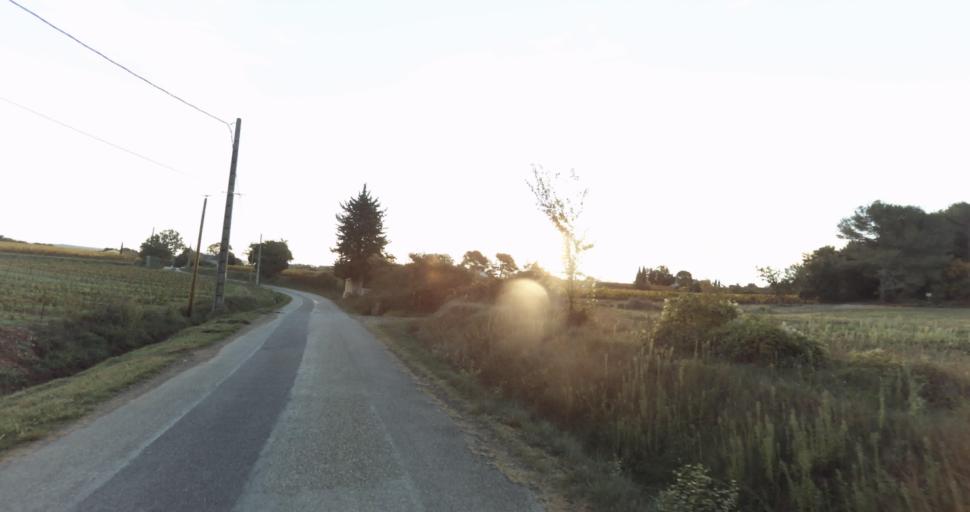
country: FR
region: Provence-Alpes-Cote d'Azur
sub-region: Departement des Bouches-du-Rhone
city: Venelles
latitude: 43.5759
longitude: 5.4898
